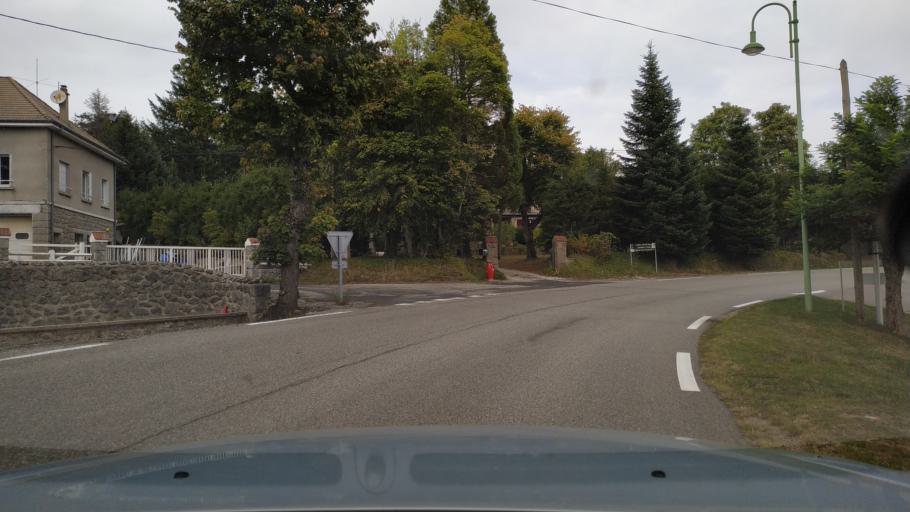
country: FR
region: Rhone-Alpes
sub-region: Departement de l'Ardeche
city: Saint-Agreve
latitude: 45.0120
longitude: 4.4011
